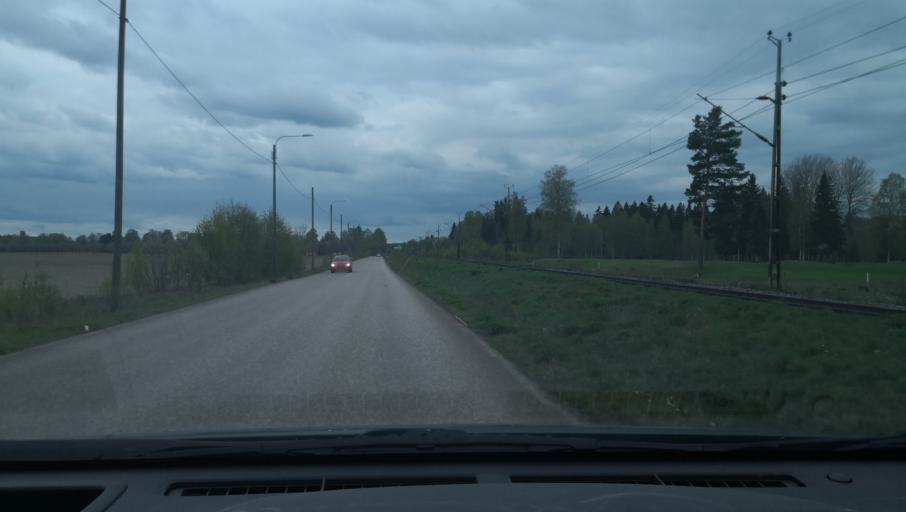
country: SE
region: Dalarna
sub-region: Avesta Kommun
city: Avesta
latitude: 60.1429
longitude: 16.2235
